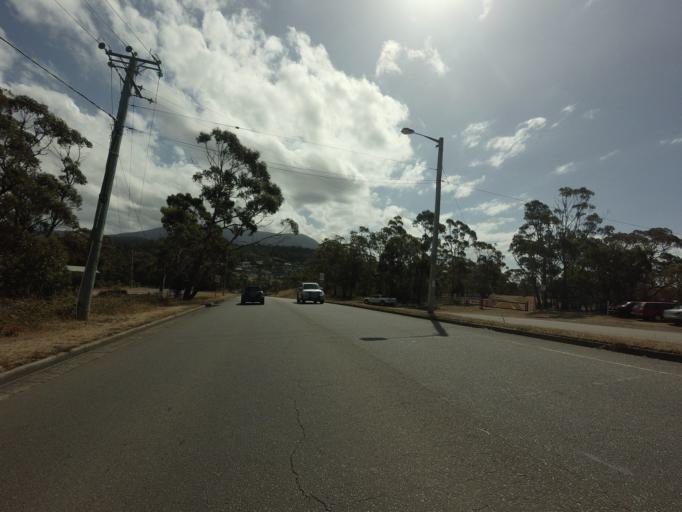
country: AU
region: Tasmania
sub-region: Hobart
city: Dynnyrne
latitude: -42.9144
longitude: 147.3149
